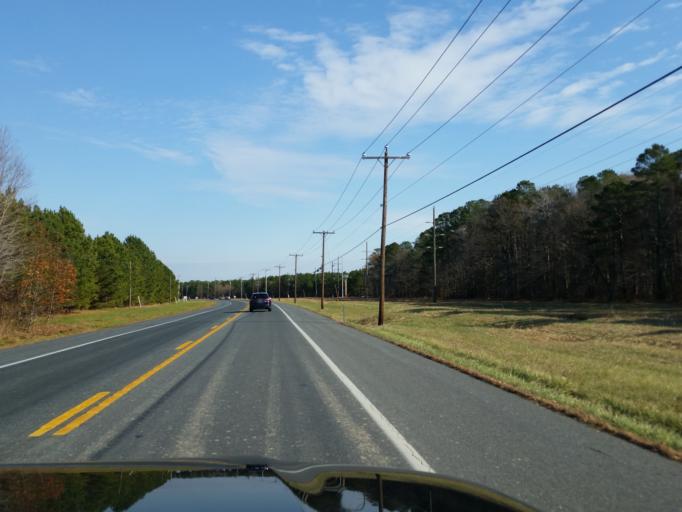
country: US
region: Maryland
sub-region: Talbot County
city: Saint Michaels
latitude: 38.7547
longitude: -76.1599
